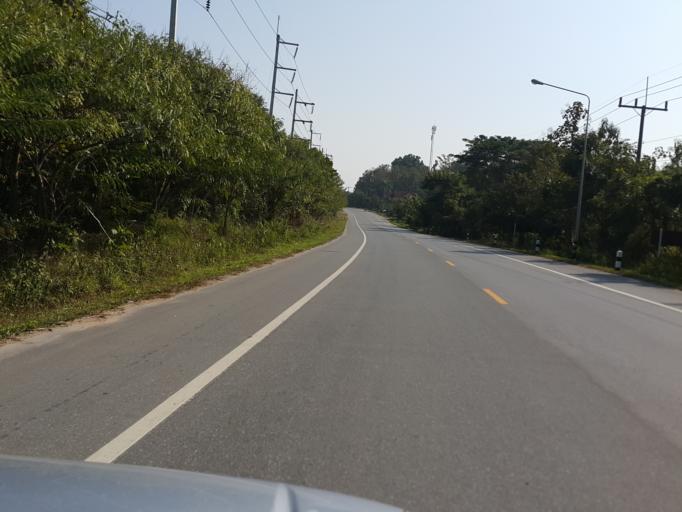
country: TH
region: Lampang
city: Chae Hom
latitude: 18.6498
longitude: 99.5373
